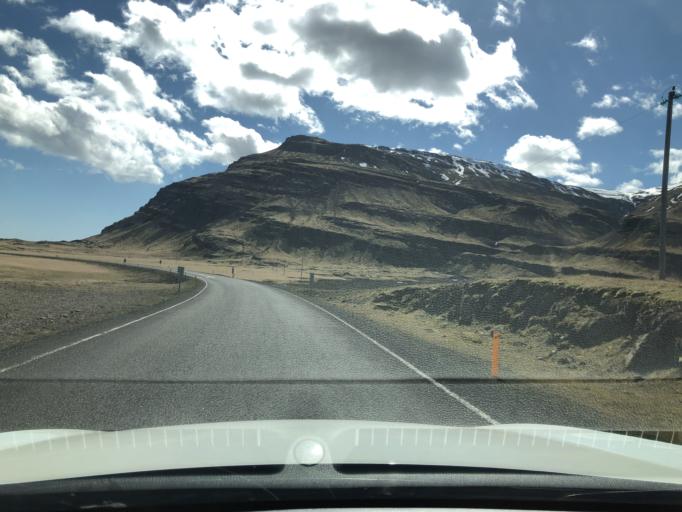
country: IS
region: East
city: Reydarfjoerdur
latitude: 64.5491
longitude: -14.6112
